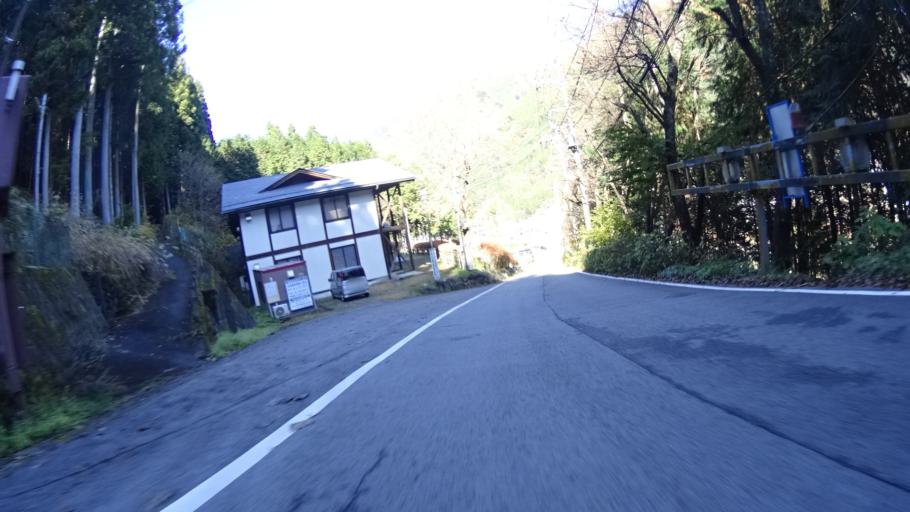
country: JP
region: Yamanashi
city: Otsuki
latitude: 35.7854
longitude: 138.9225
